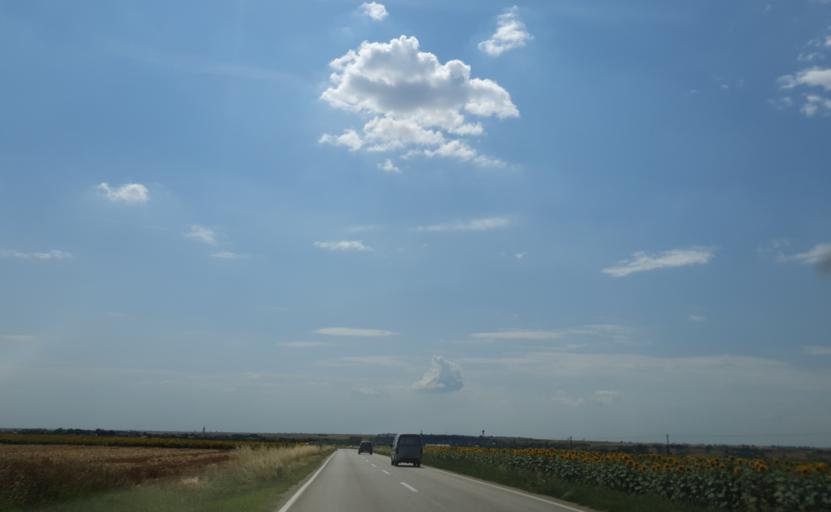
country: TR
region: Tekirdag
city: Beyazkoy
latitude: 41.4459
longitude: 27.6078
